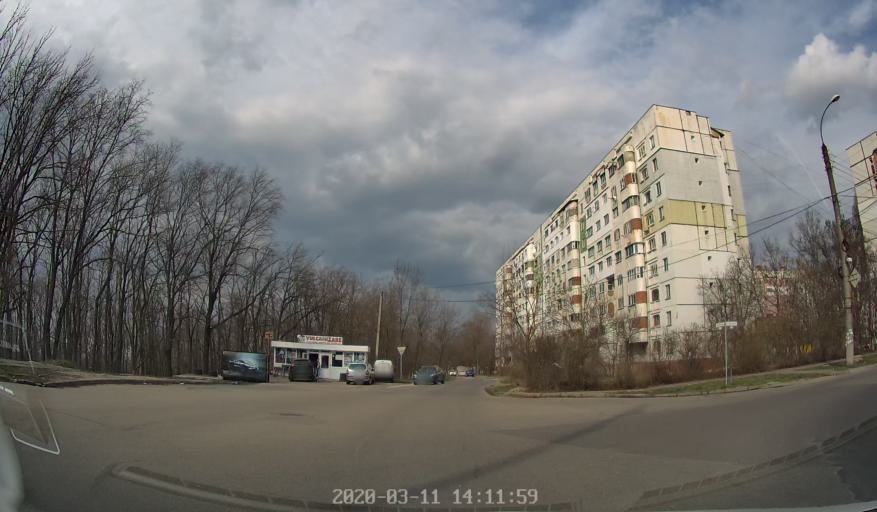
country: MD
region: Chisinau
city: Stauceni
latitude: 47.0502
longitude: 28.8835
